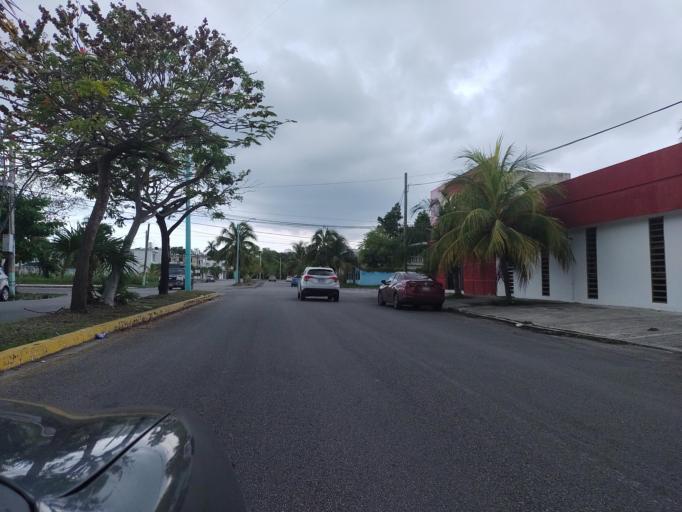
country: MX
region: Quintana Roo
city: Chetumal
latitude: 18.5048
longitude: -88.2851
